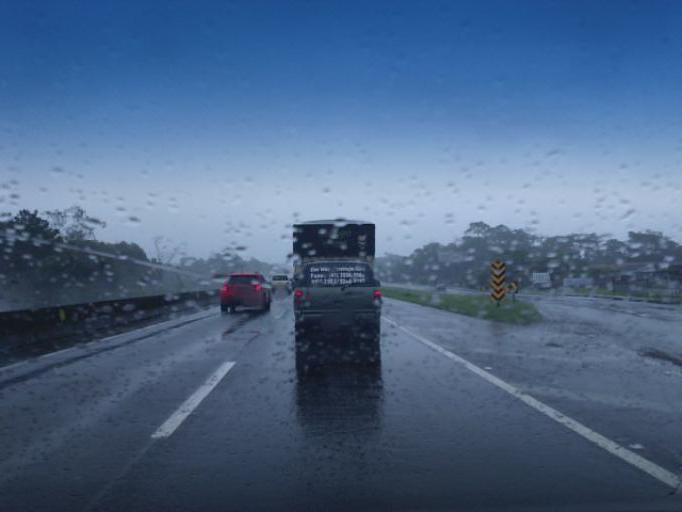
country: BR
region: Santa Catarina
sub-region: Joinville
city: Joinville
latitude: -26.0371
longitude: -48.8600
